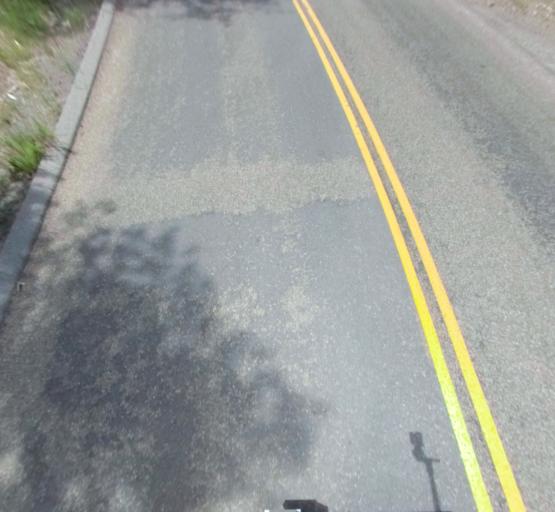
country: US
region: California
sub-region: Madera County
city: Oakhurst
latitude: 37.4505
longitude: -119.4653
